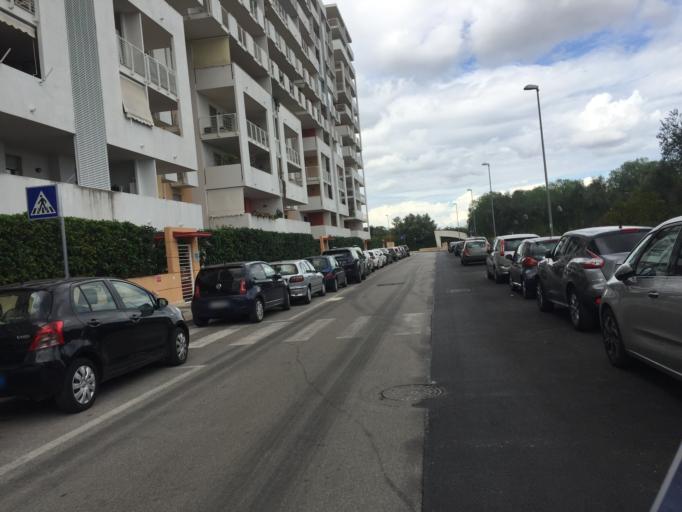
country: IT
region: Apulia
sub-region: Provincia di Bari
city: Bari
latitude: 41.1007
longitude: 16.8445
